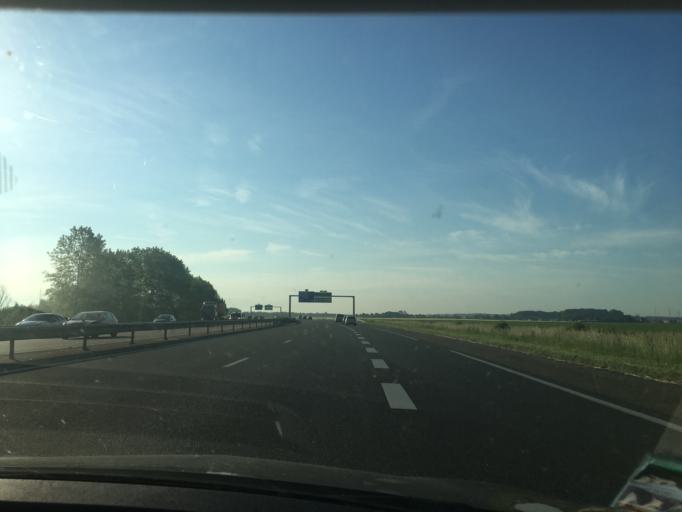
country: FR
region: Ile-de-France
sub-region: Departement de Seine-et-Marne
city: Vert-Saint-Denis
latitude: 48.5953
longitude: 2.6130
